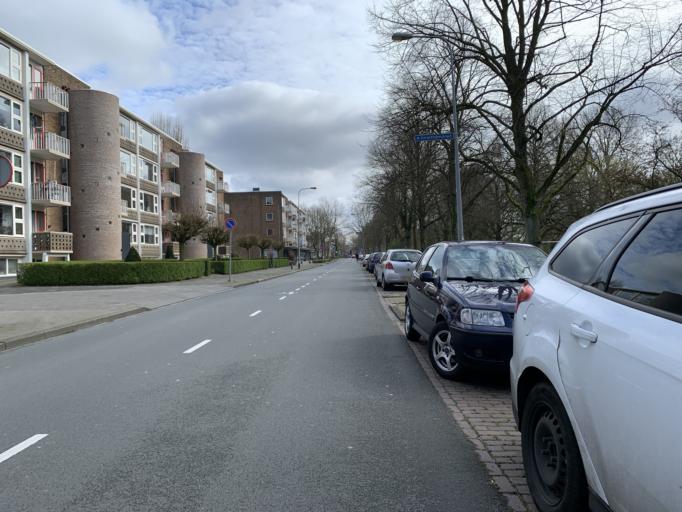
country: NL
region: Groningen
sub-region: Gemeente Groningen
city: Korrewegwijk
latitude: 53.2358
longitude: 6.5712
